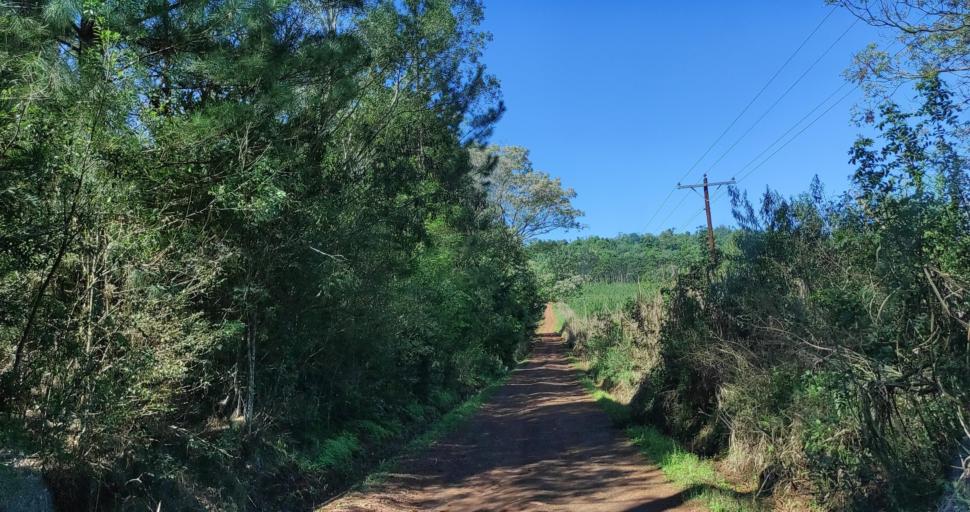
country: AR
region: Misiones
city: Capiovi
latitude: -26.9346
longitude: -54.9982
